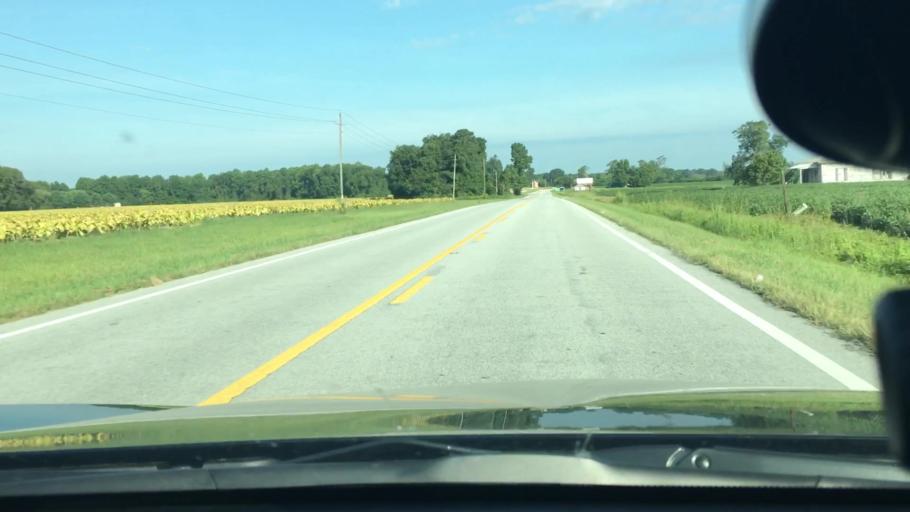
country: US
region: North Carolina
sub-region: Pitt County
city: Farmville
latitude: 35.6698
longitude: -77.4812
